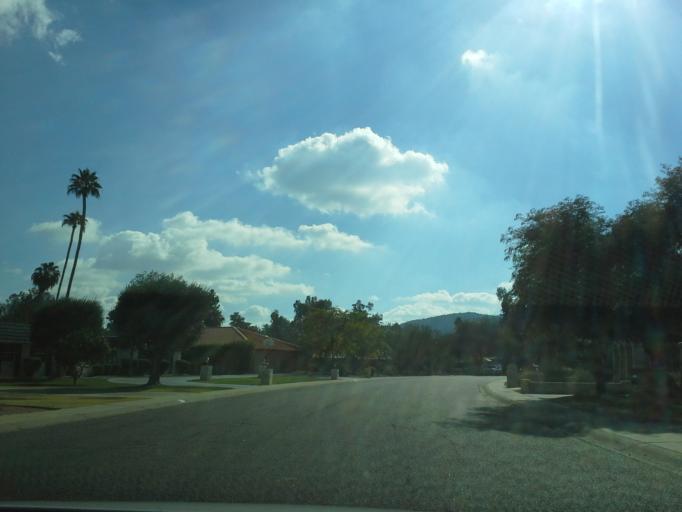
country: US
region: Arizona
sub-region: Maricopa County
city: Glendale
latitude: 33.6163
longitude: -112.0824
